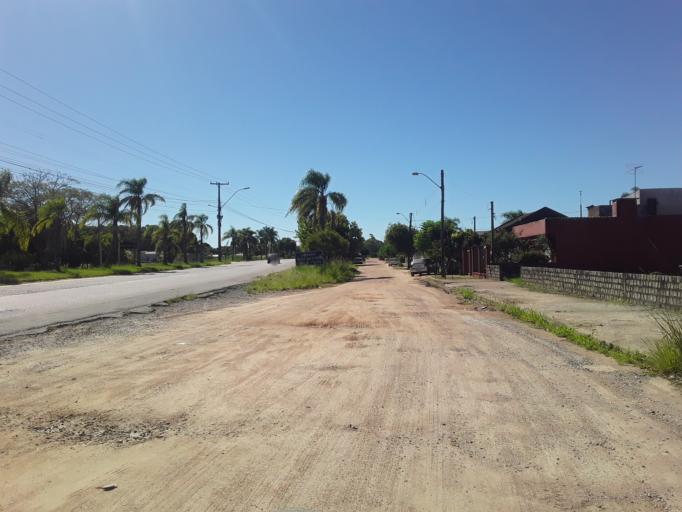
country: BR
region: Rio Grande do Sul
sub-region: Sao Lourenco Do Sul
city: Sao Lourenco do Sul
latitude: -31.3485
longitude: -51.9922
